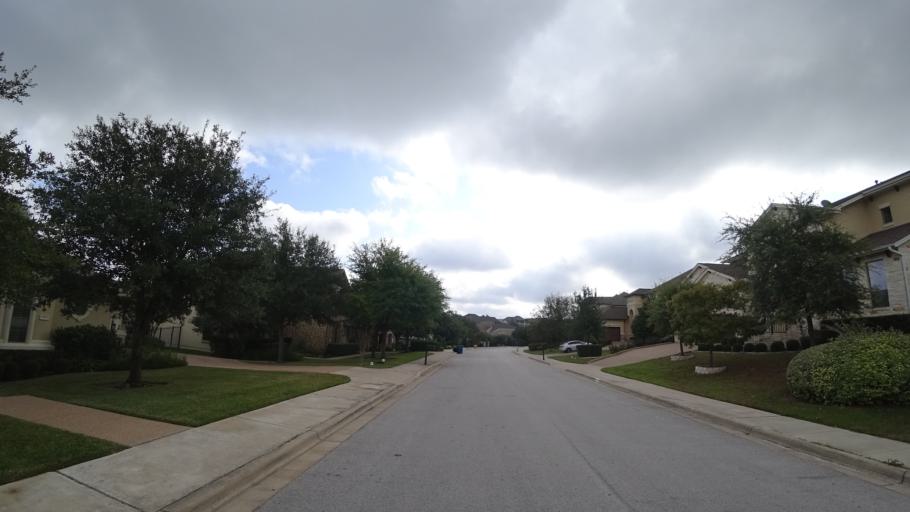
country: US
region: Texas
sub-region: Travis County
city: Barton Creek
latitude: 30.3169
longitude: -97.8992
